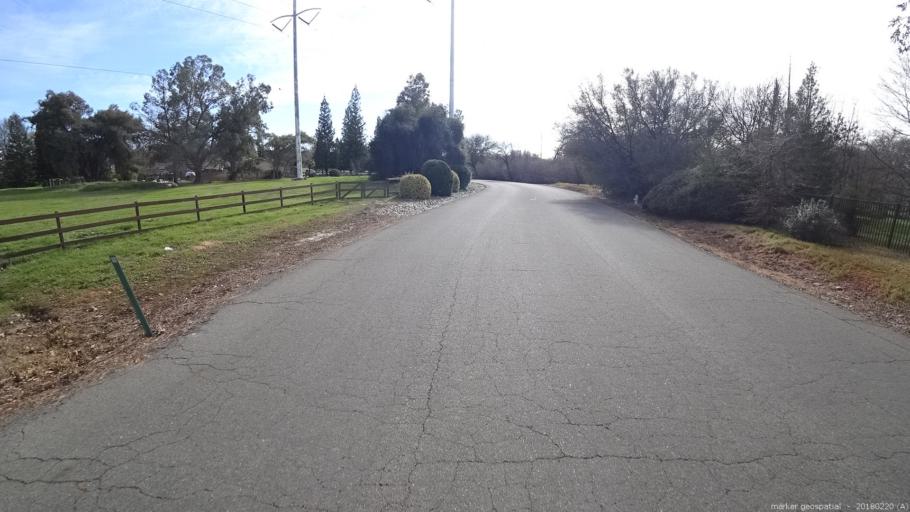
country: US
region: California
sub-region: Sacramento County
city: Orangevale
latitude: 38.7118
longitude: -121.2354
